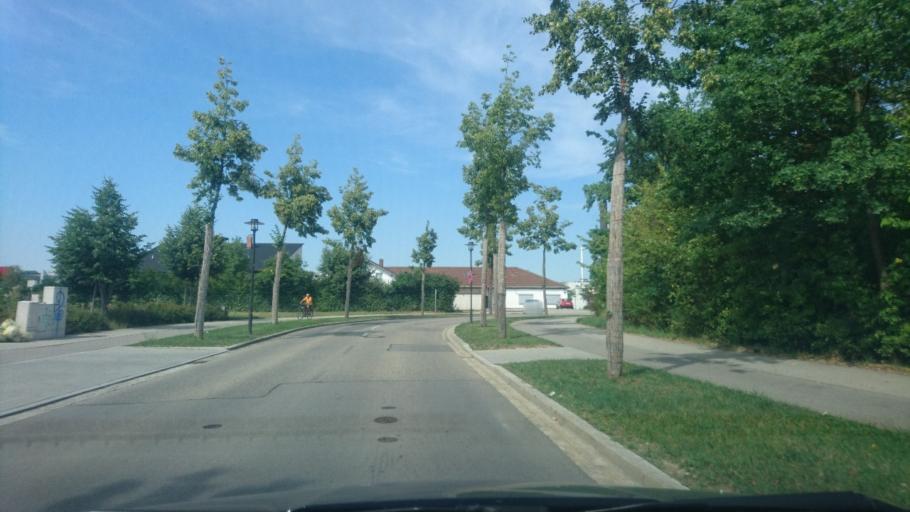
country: DE
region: Bavaria
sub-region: Upper Palatinate
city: Sinzing
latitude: 49.0198
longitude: 12.0549
